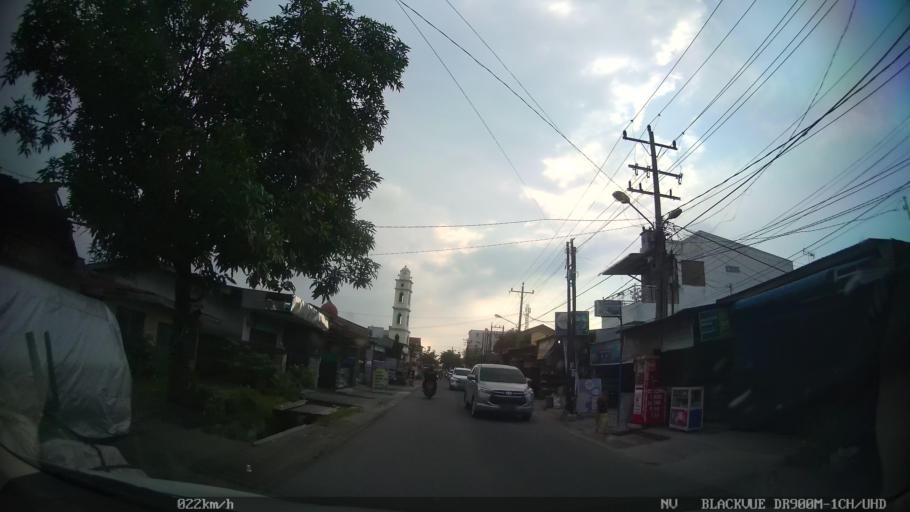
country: ID
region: North Sumatra
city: Medan
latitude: 3.6096
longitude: 98.6930
